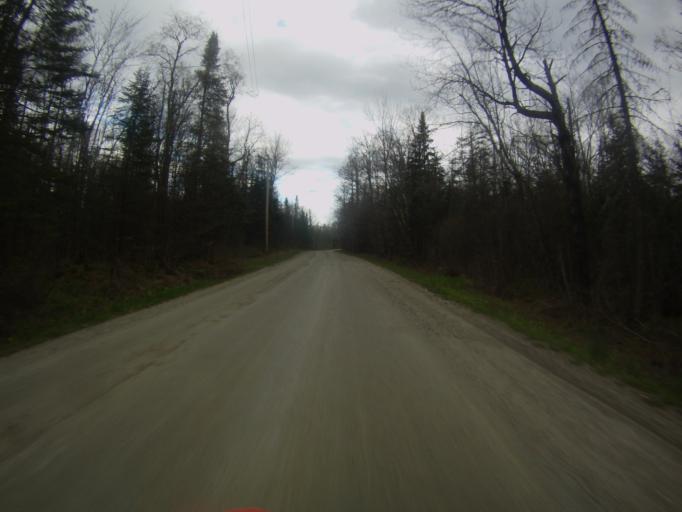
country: US
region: Vermont
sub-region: Addison County
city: Bristol
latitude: 44.0343
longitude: -73.0178
